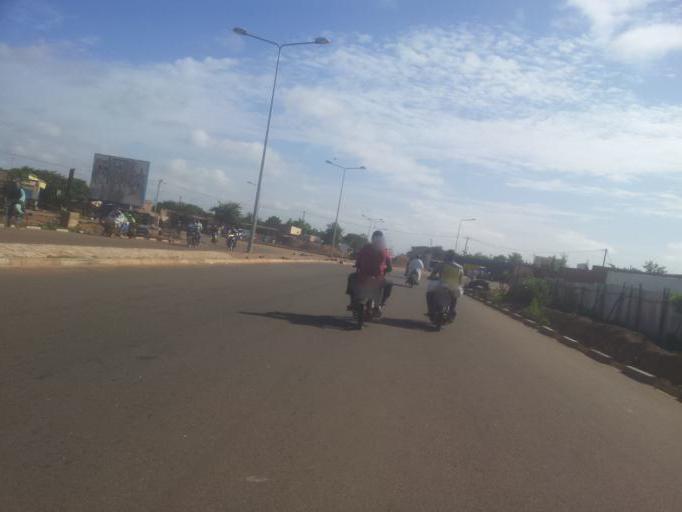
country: BF
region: Centre
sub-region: Kadiogo Province
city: Ouagadougou
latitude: 12.3830
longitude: -1.5696
